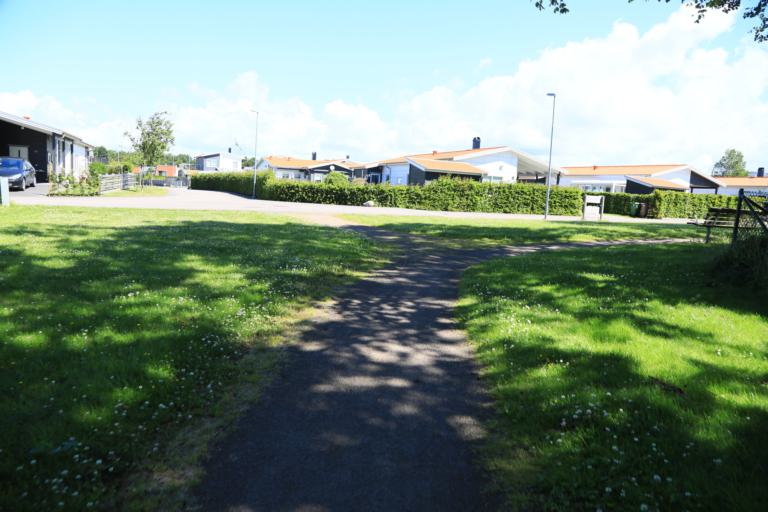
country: SE
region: Halland
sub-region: Varbergs Kommun
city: Varberg
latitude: 57.1296
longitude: 12.2684
